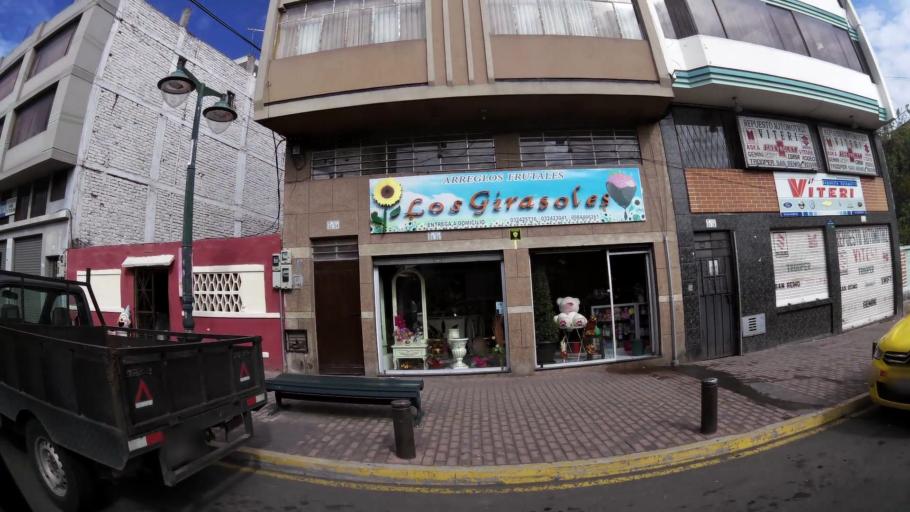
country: EC
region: Tungurahua
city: Ambato
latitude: -1.2304
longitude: -78.6285
